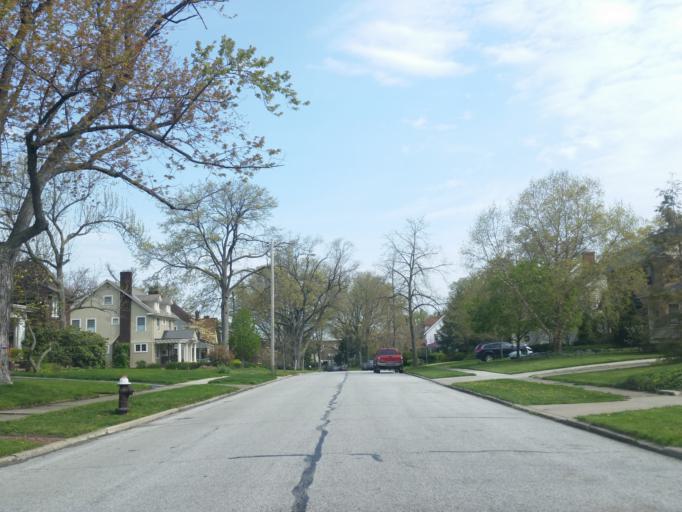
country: US
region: Ohio
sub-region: Cuyahoga County
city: Lakewood
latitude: 41.4815
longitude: -81.7829
